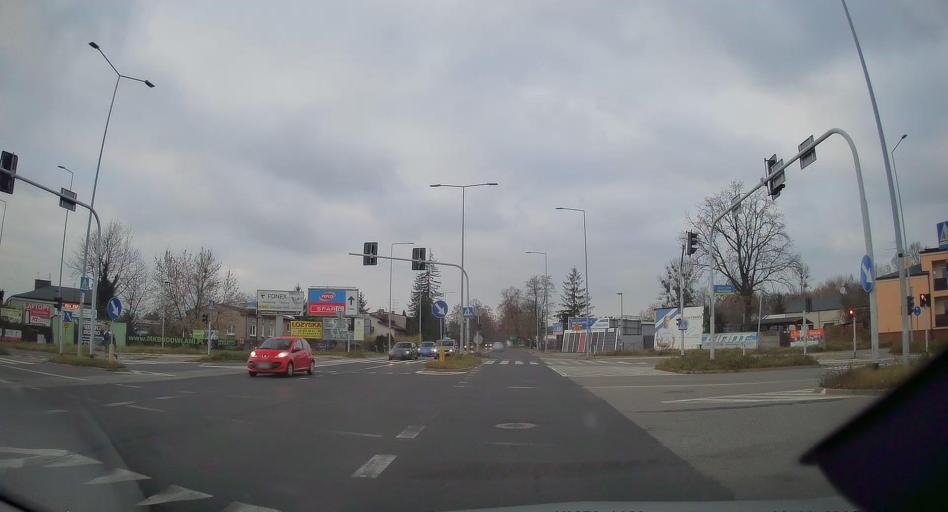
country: PL
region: Silesian Voivodeship
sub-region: Czestochowa
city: Czestochowa
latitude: 50.8225
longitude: 19.0821
